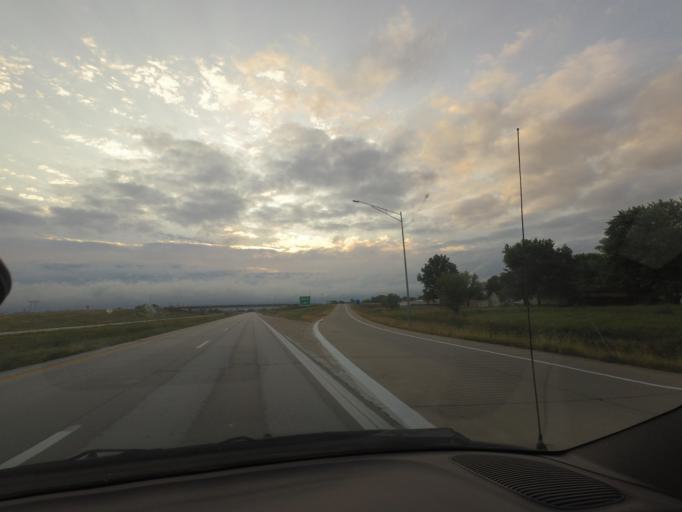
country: US
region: Missouri
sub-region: Shelby County
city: Shelbina
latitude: 39.6979
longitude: -92.0428
